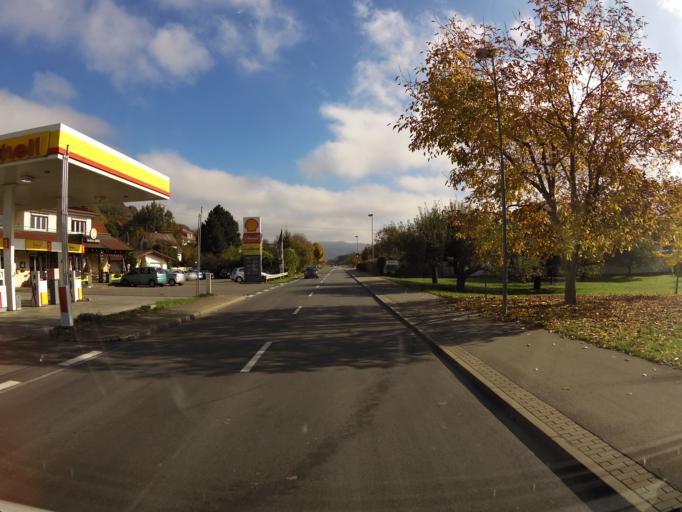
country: DE
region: Baden-Wuerttemberg
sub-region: Freiburg Region
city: Stockach
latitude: 47.8185
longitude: 9.0131
